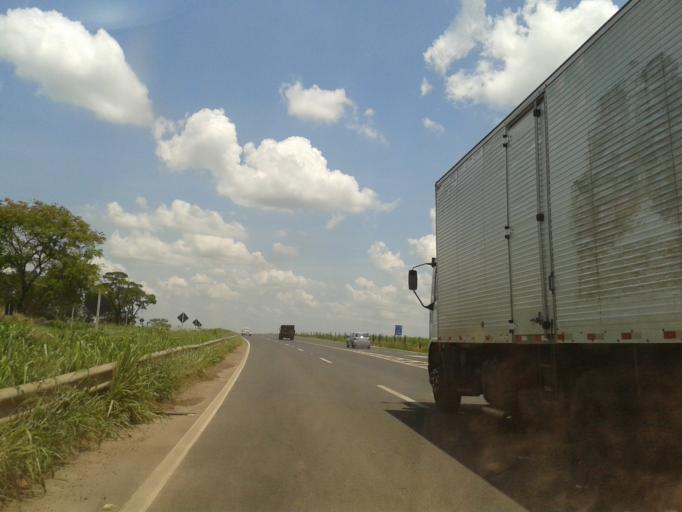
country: BR
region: Minas Gerais
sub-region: Monte Alegre De Minas
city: Monte Alegre de Minas
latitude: -18.8646
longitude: -48.5890
